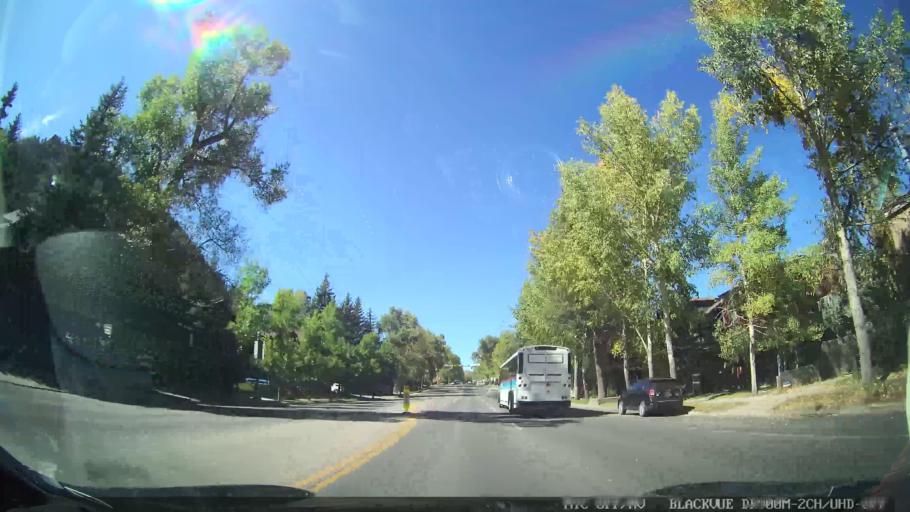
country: US
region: Colorado
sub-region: Pitkin County
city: Aspen
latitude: 39.1917
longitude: -106.8239
